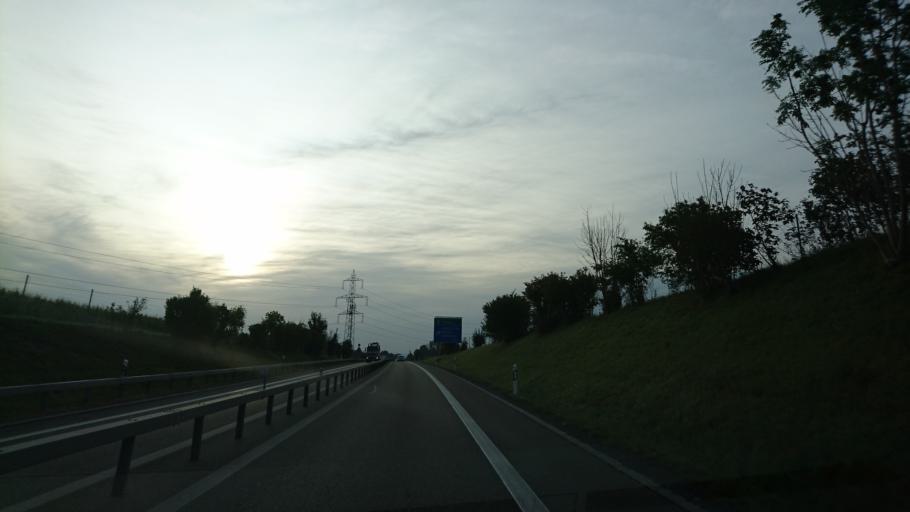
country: CH
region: Zurich
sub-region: Bezirk Uster
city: Esslingen
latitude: 47.2902
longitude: 8.7217
